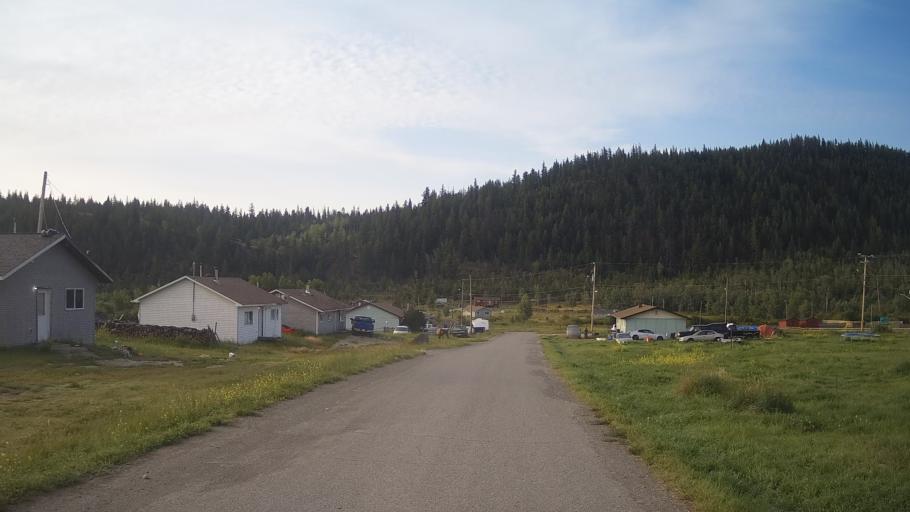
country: CA
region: British Columbia
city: Hanceville
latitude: 52.1380
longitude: -123.9514
